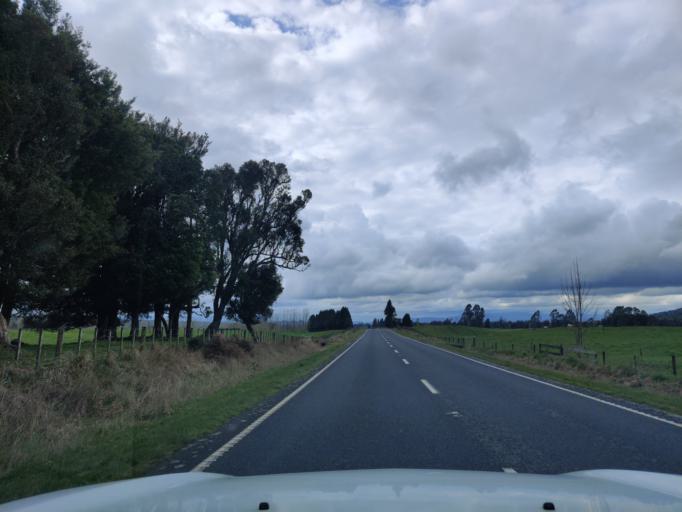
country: NZ
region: Waikato
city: Turangi
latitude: -39.0384
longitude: 175.3831
